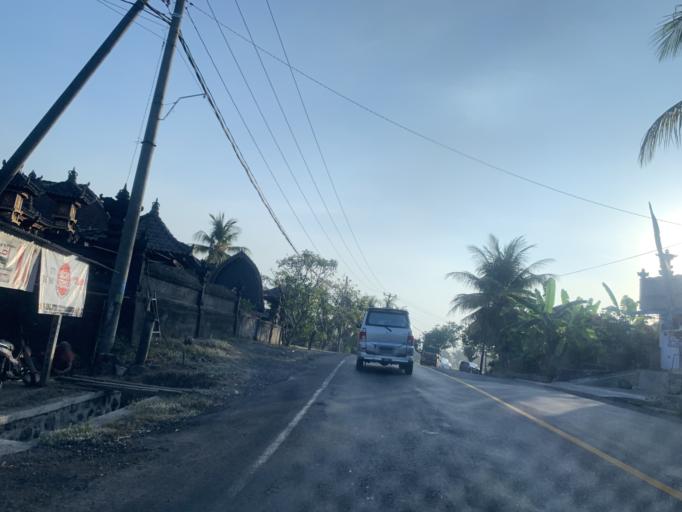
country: ID
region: Bali
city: Angkahgede
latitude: -8.4775
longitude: 114.9395
